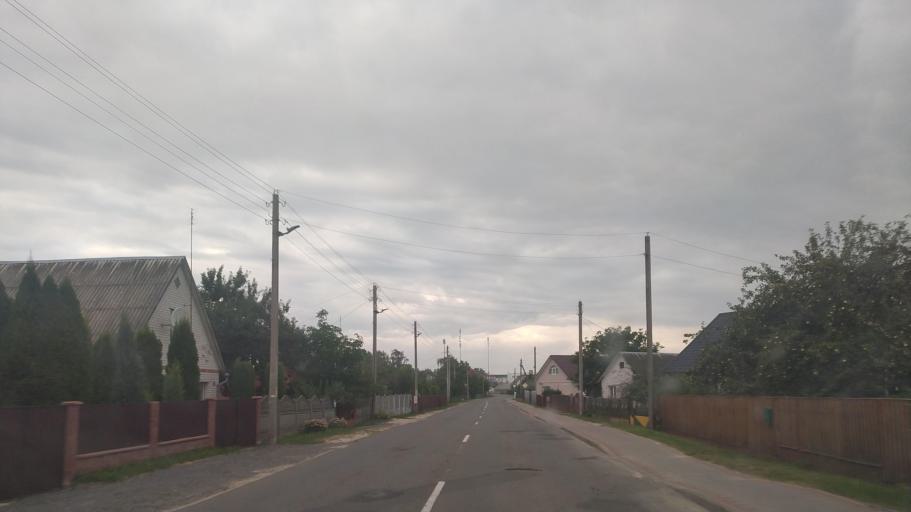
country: BY
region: Brest
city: Byaroza
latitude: 52.5251
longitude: 24.9741
